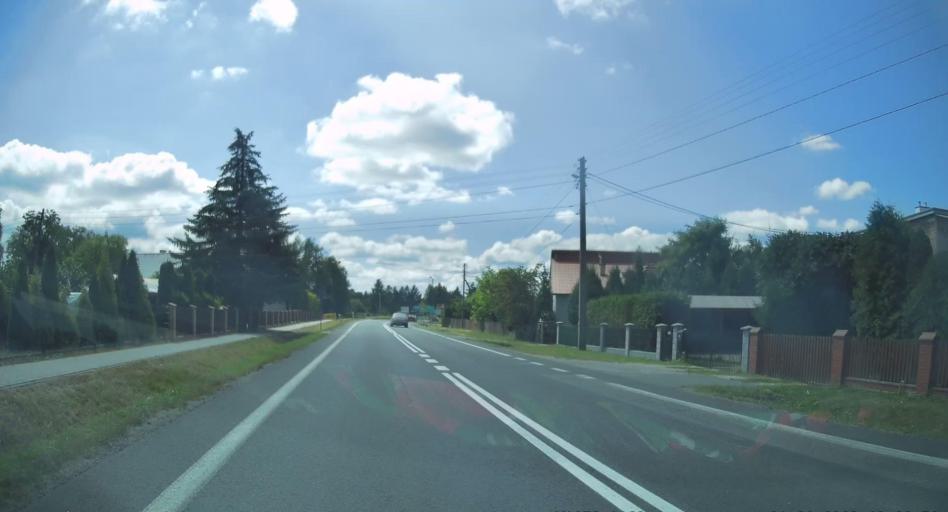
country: PL
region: Subcarpathian Voivodeship
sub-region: Powiat debicki
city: Brzeznica
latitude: 50.1110
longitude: 21.4900
